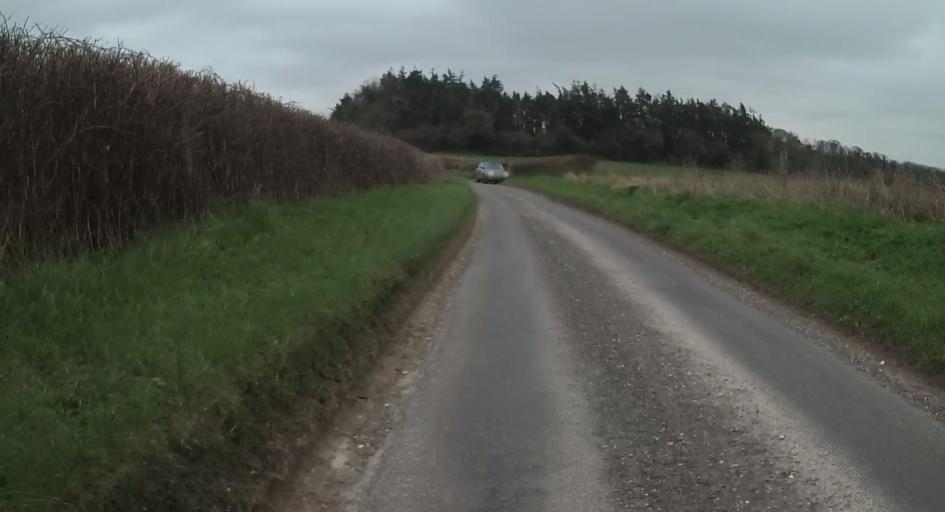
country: GB
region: England
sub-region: Hampshire
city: Four Marks
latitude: 51.1108
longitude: -1.1333
